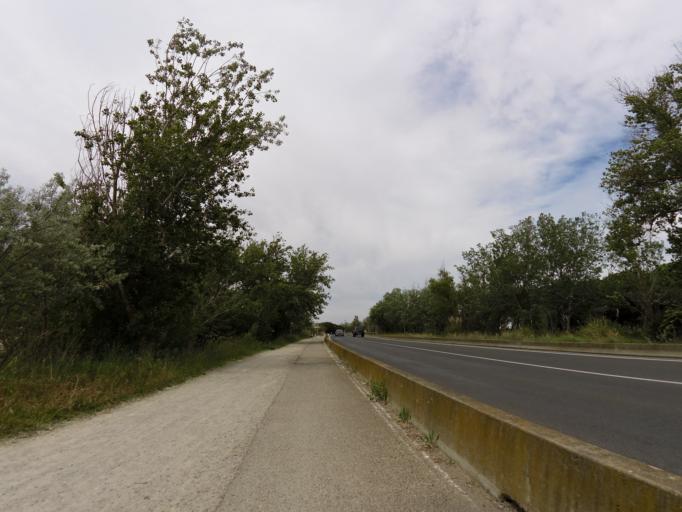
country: FR
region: Languedoc-Roussillon
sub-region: Departement de l'Herault
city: La Grande-Motte
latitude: 43.5557
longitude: 4.1033
